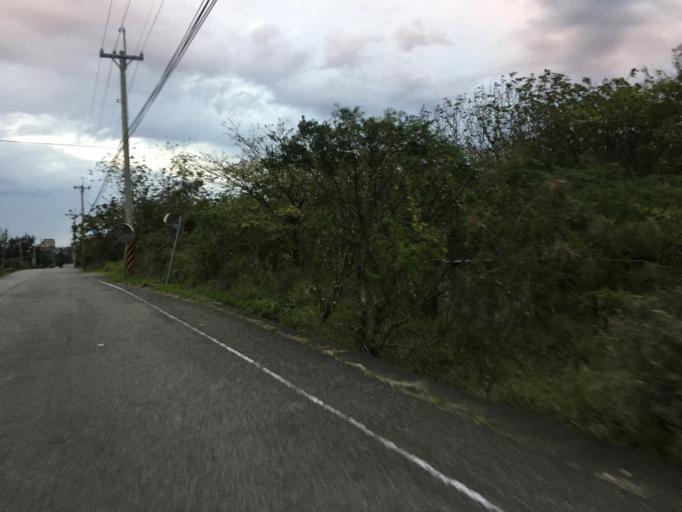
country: TW
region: Taiwan
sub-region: Hsinchu
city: Hsinchu
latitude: 24.7362
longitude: 120.8884
